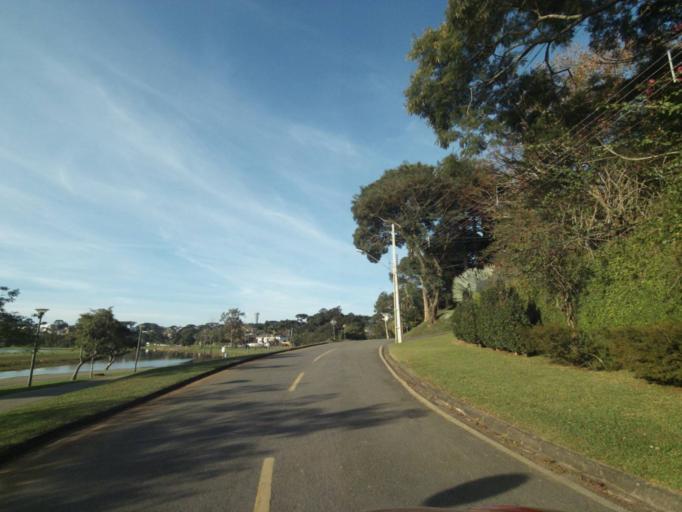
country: BR
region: Parana
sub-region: Curitiba
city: Curitiba
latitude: -25.4315
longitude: -49.3098
